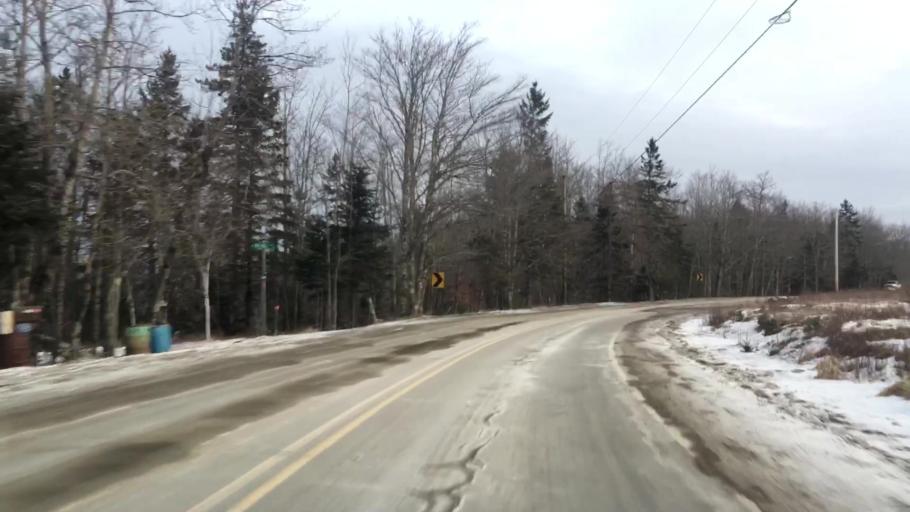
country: US
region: Maine
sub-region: Hancock County
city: Franklin
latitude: 44.7346
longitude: -68.3360
